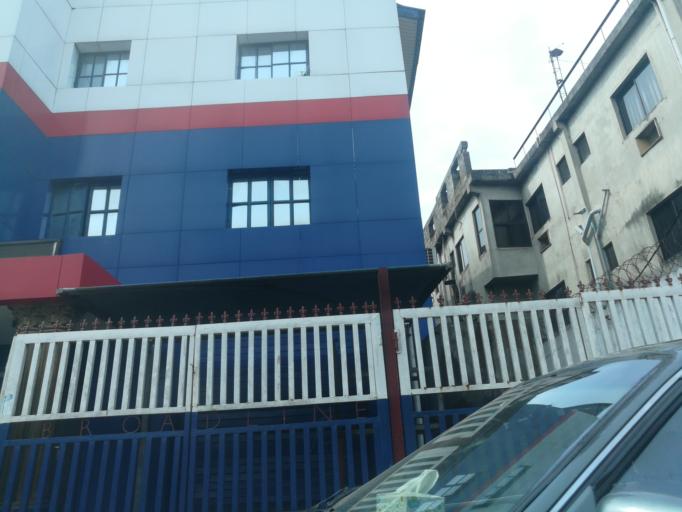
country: NG
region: Lagos
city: Ikeja
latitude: 6.5972
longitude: 3.3363
